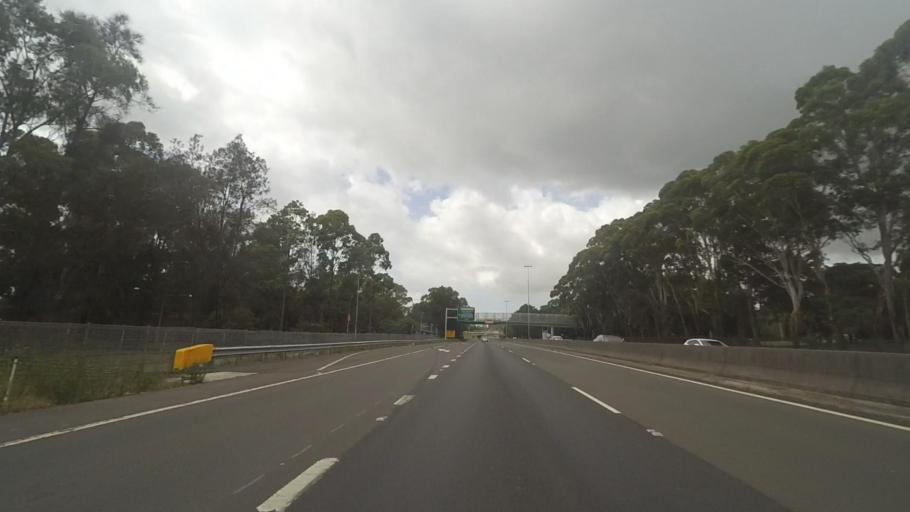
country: AU
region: New South Wales
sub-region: Wollongong
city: Gwynneville
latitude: -34.4073
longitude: 150.8836
